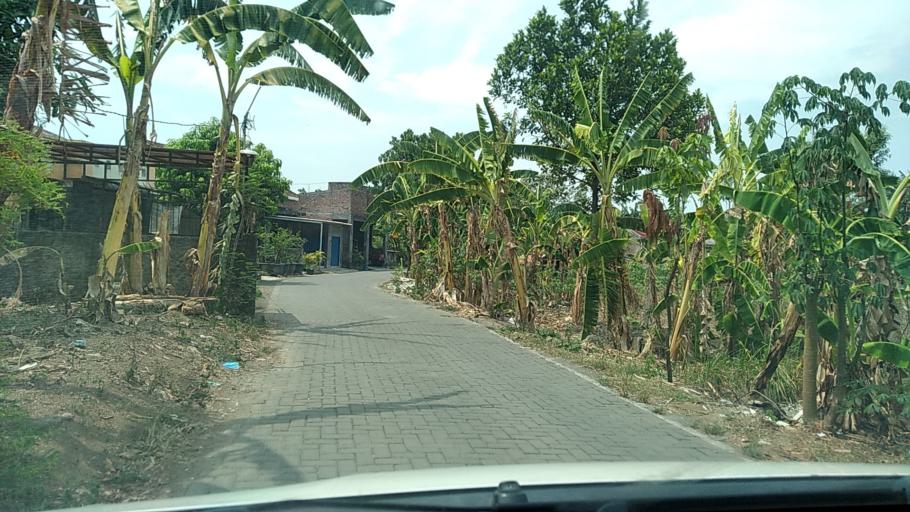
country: ID
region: Central Java
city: Mranggen
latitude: -7.0518
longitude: 110.4788
